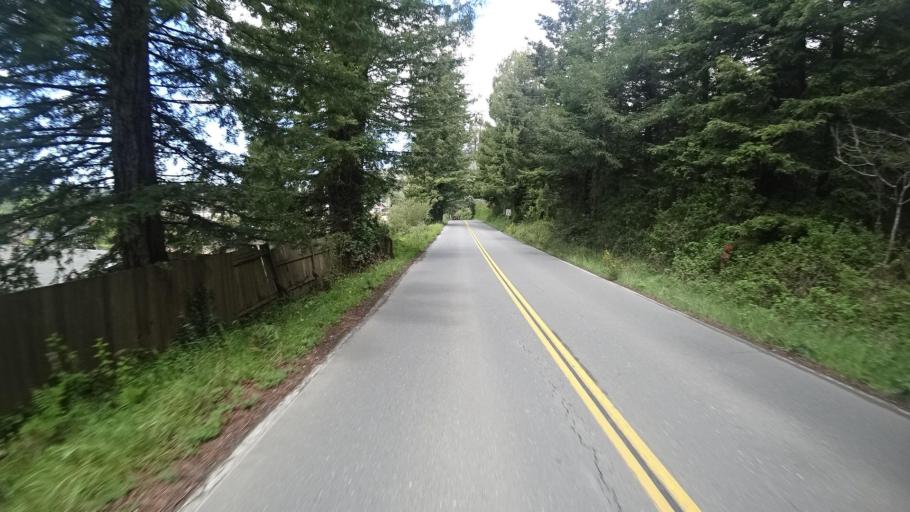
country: US
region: California
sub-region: Humboldt County
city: Blue Lake
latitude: 40.8814
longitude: -123.9790
